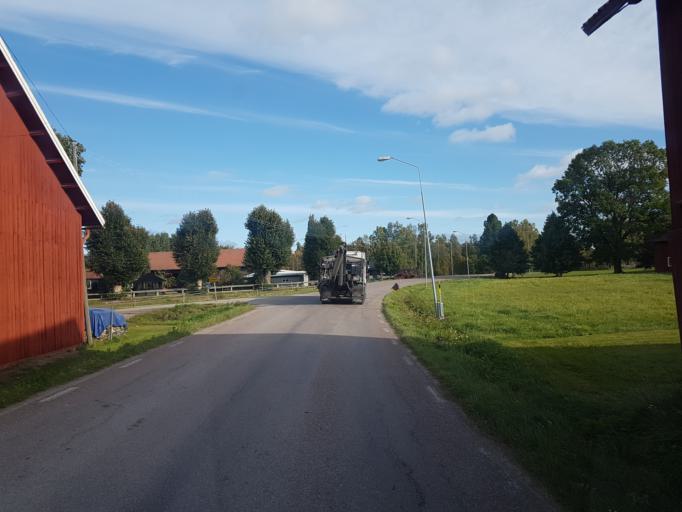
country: SE
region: Dalarna
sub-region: Saters Kommun
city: Saeter
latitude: 60.4015
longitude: 15.6356
